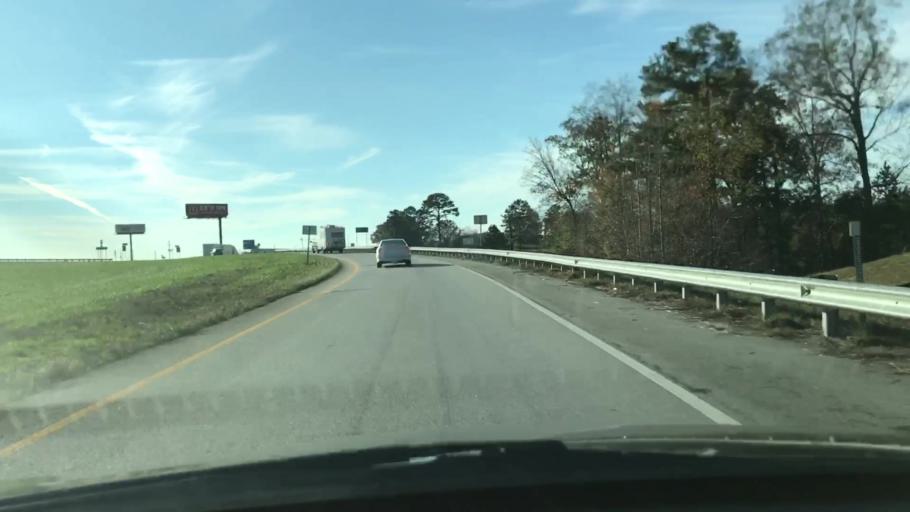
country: US
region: Alabama
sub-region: Cleburne County
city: Heflin
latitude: 33.6465
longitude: -85.5020
